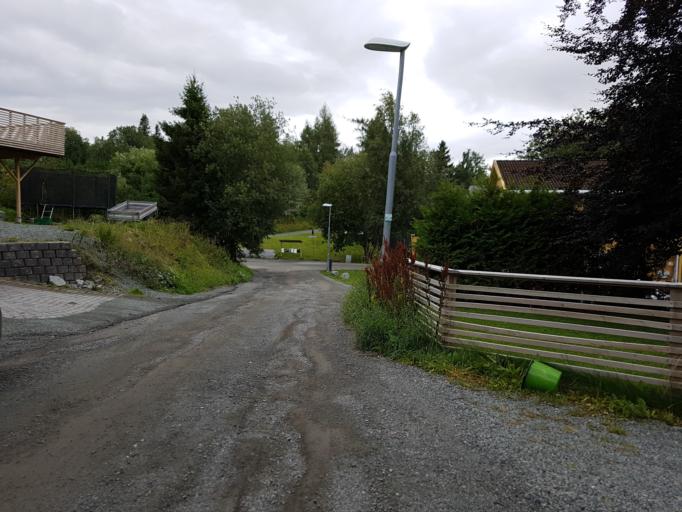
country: NO
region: Sor-Trondelag
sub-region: Trondheim
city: Trondheim
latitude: 63.4020
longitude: 10.3524
